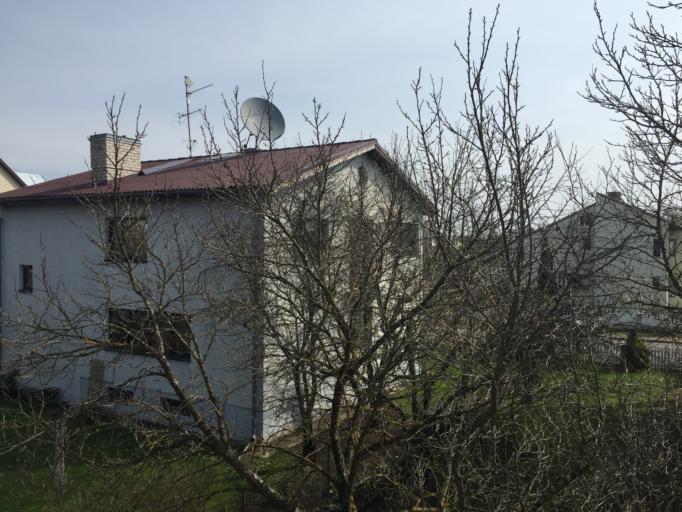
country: EE
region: Tartu
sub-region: Tartu linn
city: Tartu
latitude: 58.3686
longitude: 26.6810
